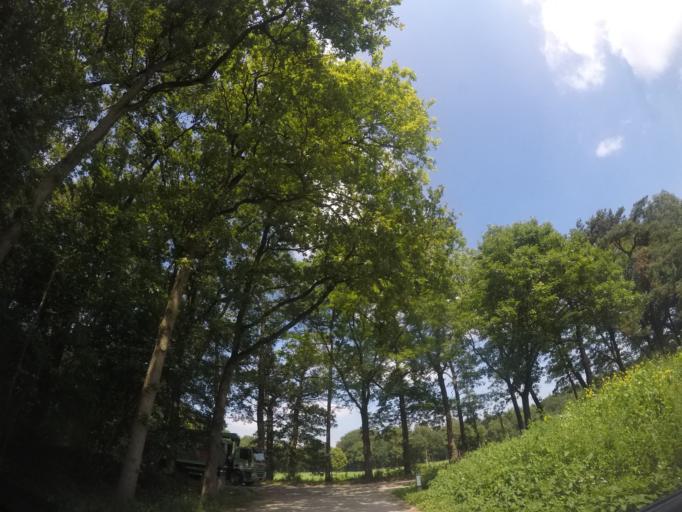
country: NL
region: Overijssel
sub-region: Gemeente Dalfsen
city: Dalfsen
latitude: 52.4820
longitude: 6.2604
